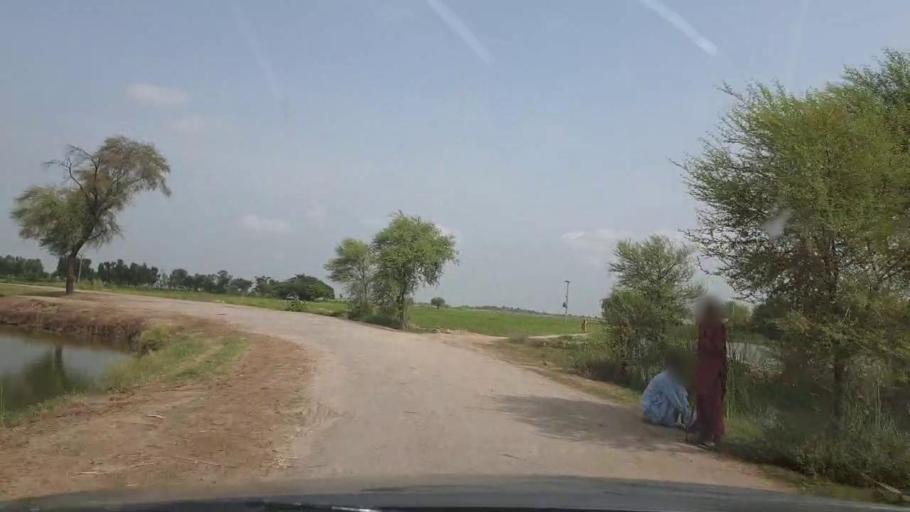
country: PK
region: Sindh
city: Ratodero
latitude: 27.8559
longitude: 68.2991
